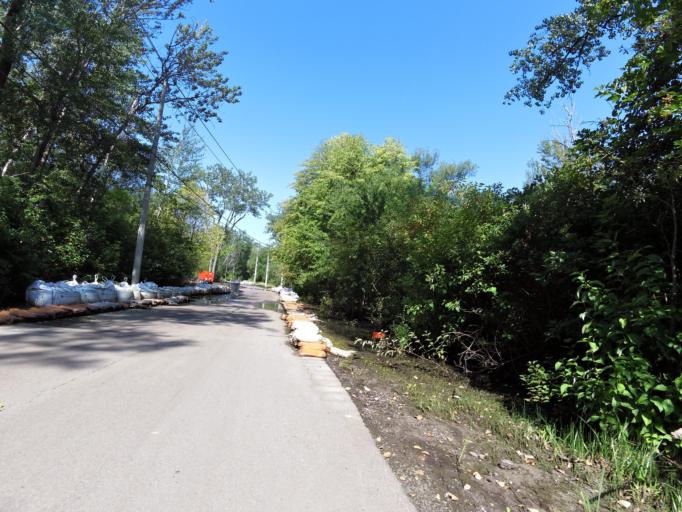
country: CA
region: Ontario
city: Toronto
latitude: 43.6131
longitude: -79.3863
